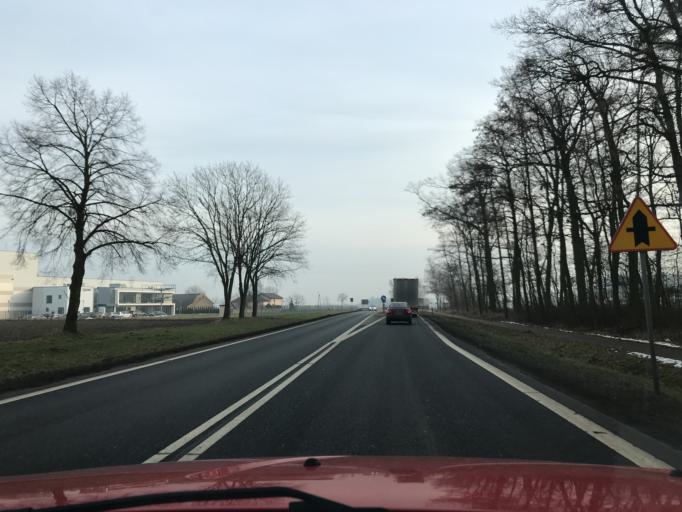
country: PL
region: Greater Poland Voivodeship
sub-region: Powiat pleszewski
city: Goluchow
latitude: 51.8226
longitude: 17.9724
